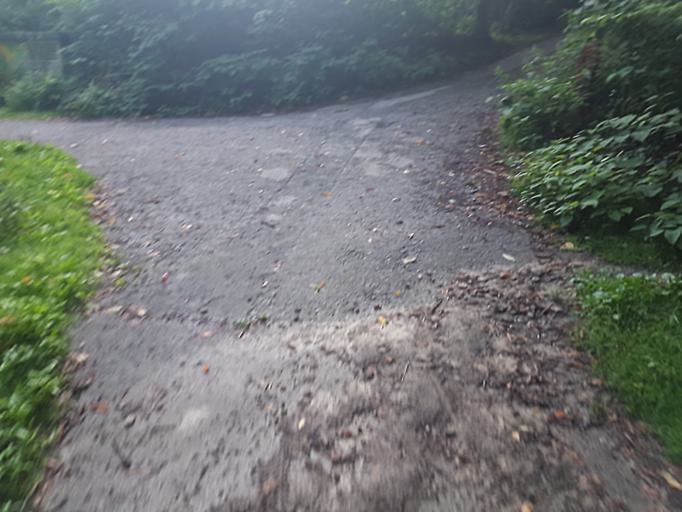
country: DE
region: North Rhine-Westphalia
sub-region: Regierungsbezirk Dusseldorf
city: Essen
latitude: 51.4106
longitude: 7.0213
